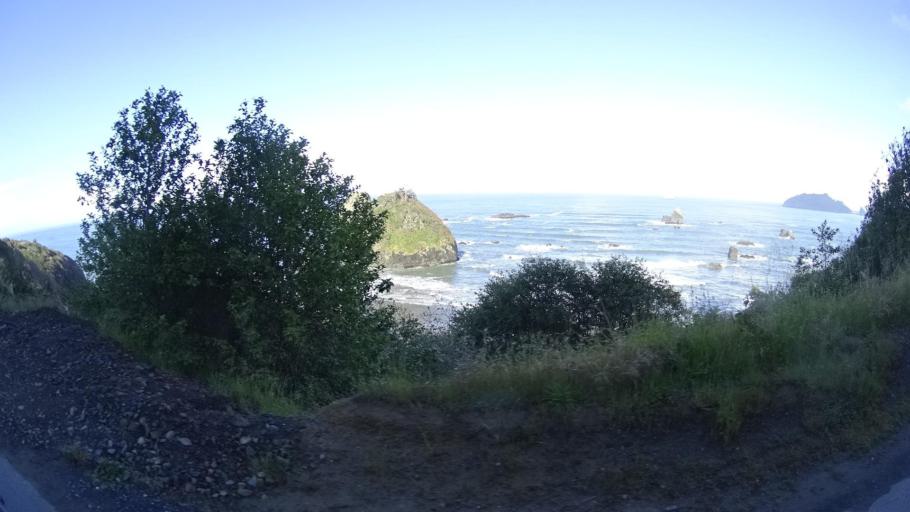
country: US
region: California
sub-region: Humboldt County
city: Westhaven-Moonstone
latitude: 41.0374
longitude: -124.1181
